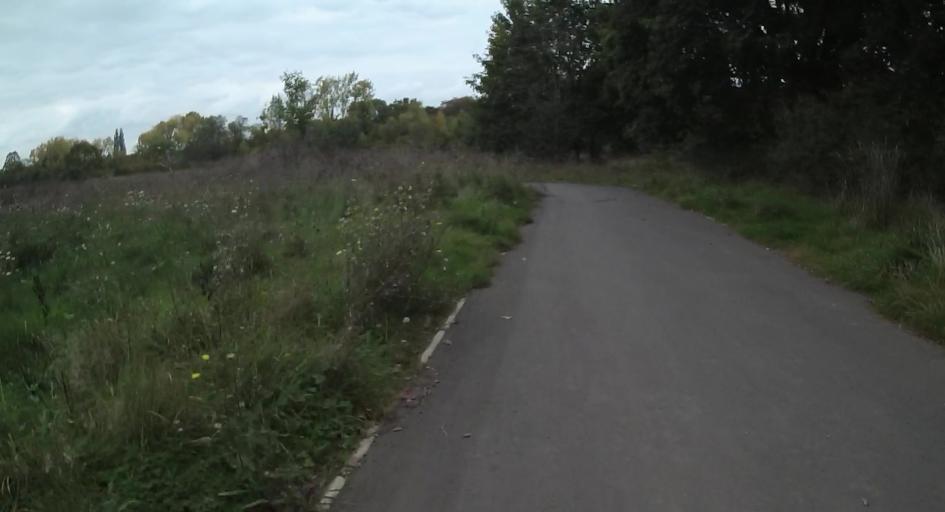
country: GB
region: England
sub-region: Bracknell Forest
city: Binfield
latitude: 51.4273
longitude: -0.7736
